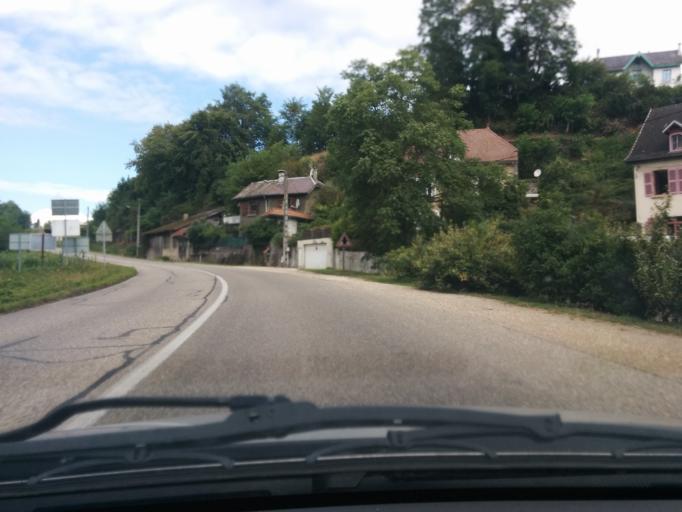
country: FR
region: Rhone-Alpes
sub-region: Departement de la Savoie
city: Le Pont-de-Beauvoisin
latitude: 45.5409
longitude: 5.6680
